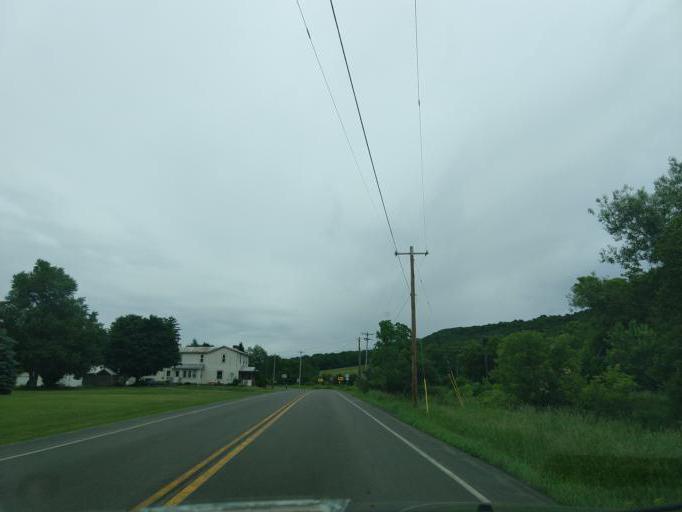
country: US
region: New York
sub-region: Cortland County
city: Munsons Corners
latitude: 42.5017
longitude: -76.2050
